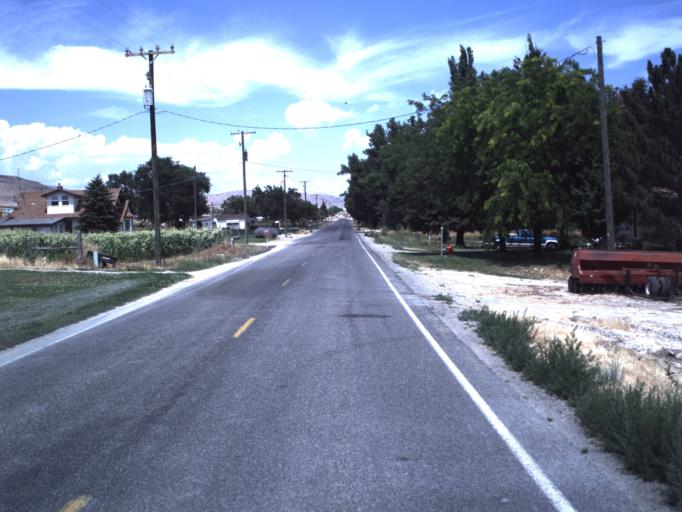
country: US
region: Utah
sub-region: Box Elder County
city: Tremonton
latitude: 41.6822
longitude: -112.2969
